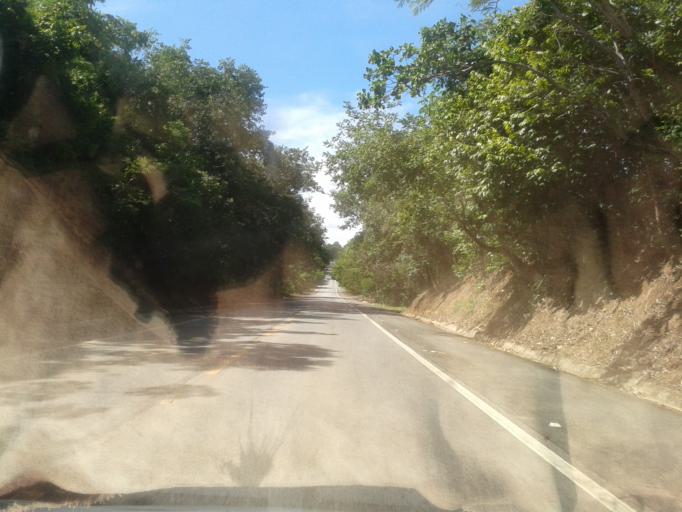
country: BR
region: Goias
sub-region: Goias
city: Goias
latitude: -15.6947
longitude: -50.1993
